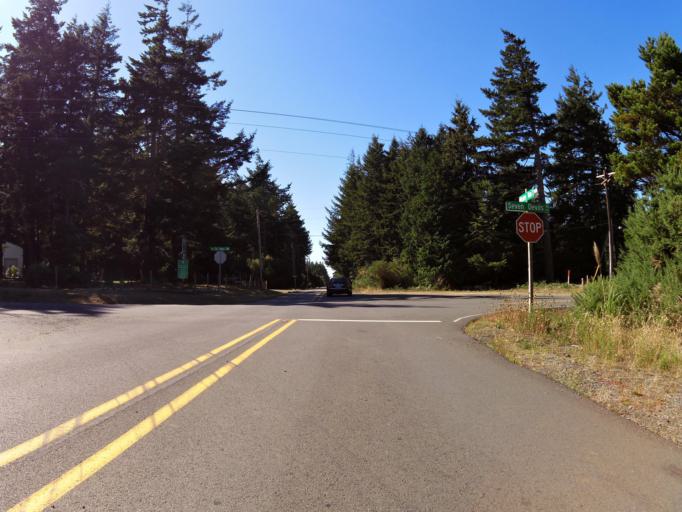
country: US
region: Oregon
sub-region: Coos County
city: Bandon
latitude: 43.2136
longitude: -124.3700
